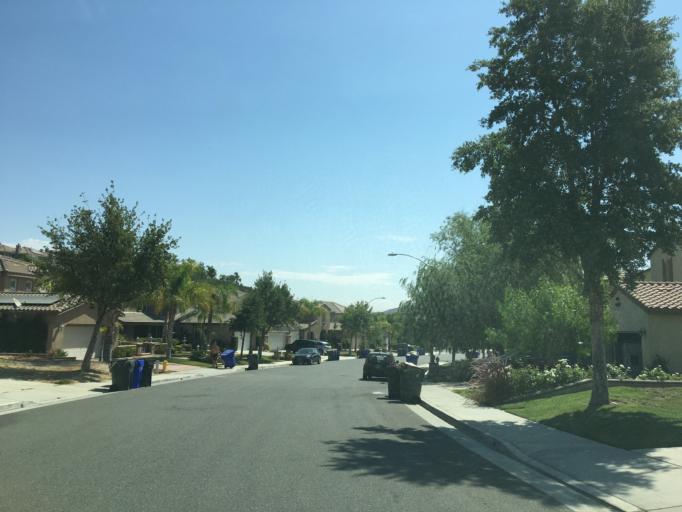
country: US
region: California
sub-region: Los Angeles County
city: Valencia
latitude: 34.4726
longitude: -118.5640
